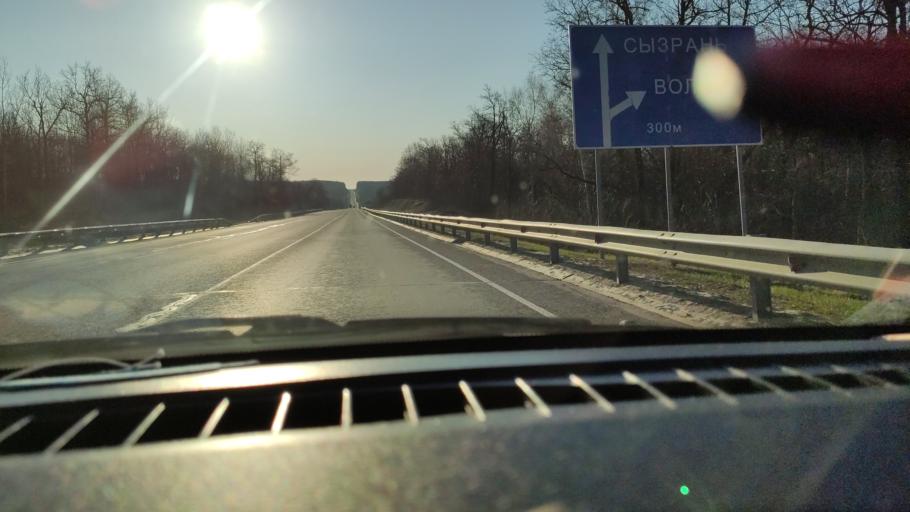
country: RU
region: Saratov
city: Vol'sk
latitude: 52.1094
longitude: 47.3713
